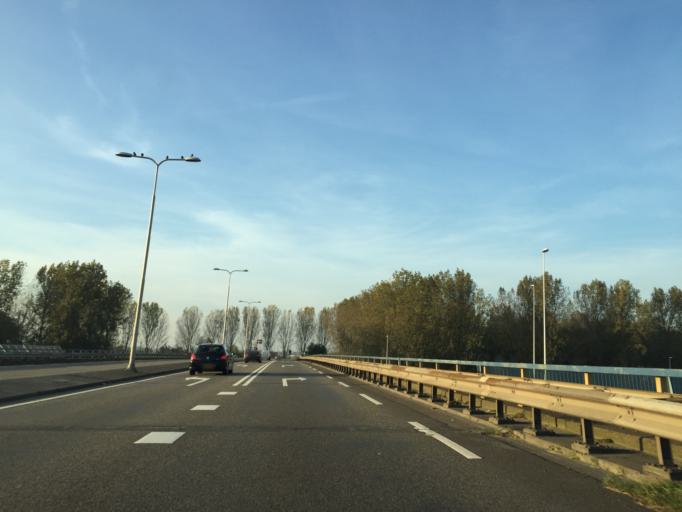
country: NL
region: South Holland
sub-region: Gemeente Gouda
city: Bloemendaal
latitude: 52.0295
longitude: 4.6838
